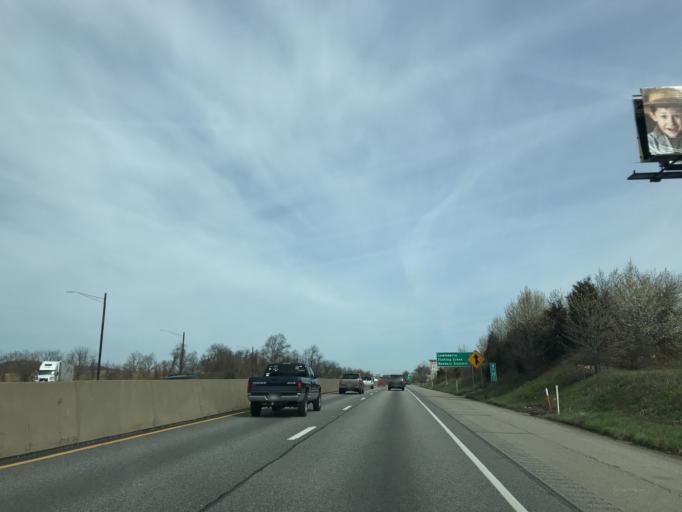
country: US
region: Pennsylvania
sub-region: York County
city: Valley Green
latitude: 40.1542
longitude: -76.8213
